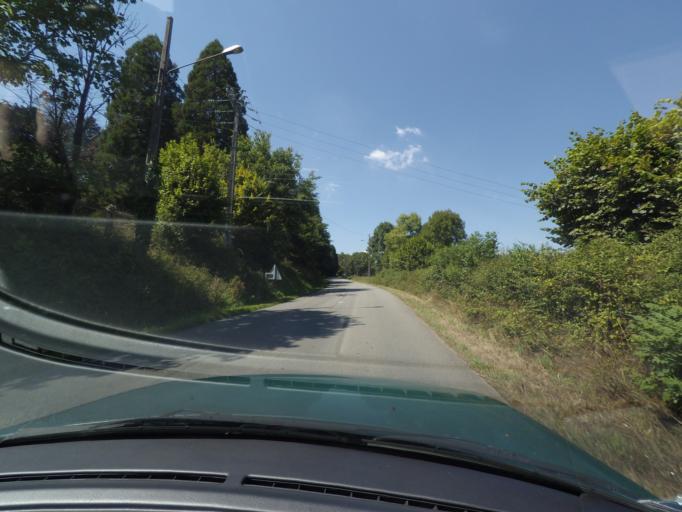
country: FR
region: Limousin
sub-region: Departement de la Haute-Vienne
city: Aixe-sur-Vienne
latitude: 45.7912
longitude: 1.1408
